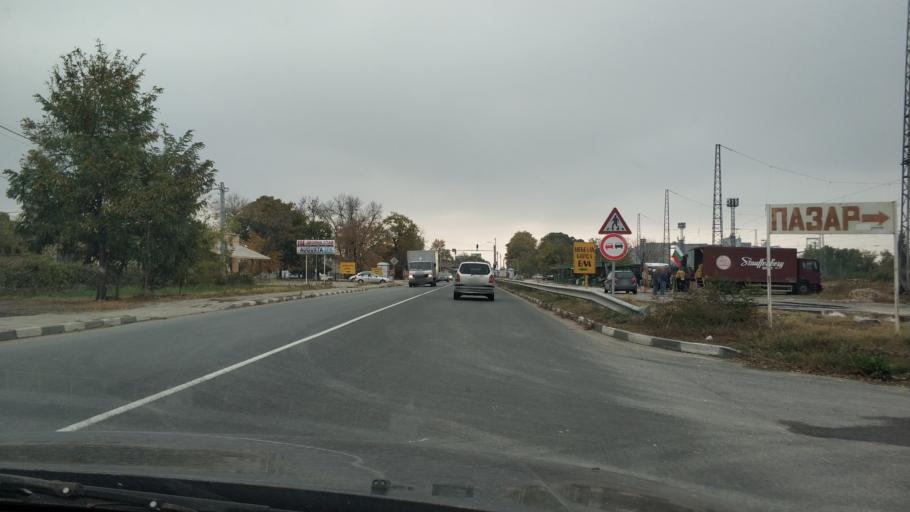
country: BG
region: Plovdiv
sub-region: Obshtina Plovdiv
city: Plovdiv
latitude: 42.2323
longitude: 24.7240
